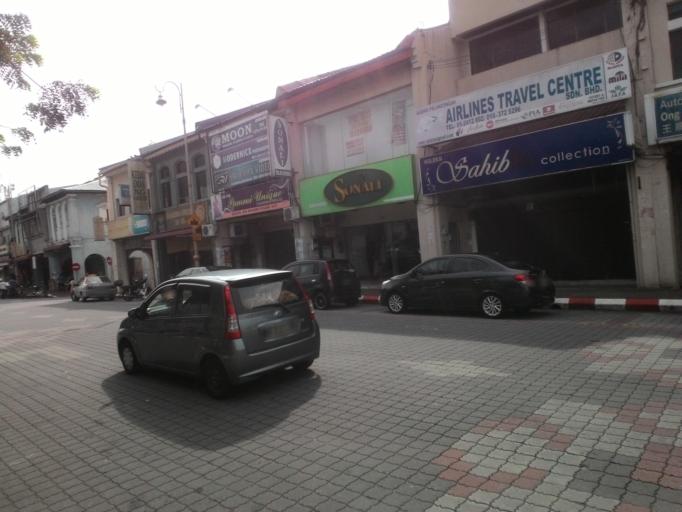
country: MY
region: Perak
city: Ipoh
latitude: 4.5935
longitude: 101.0764
